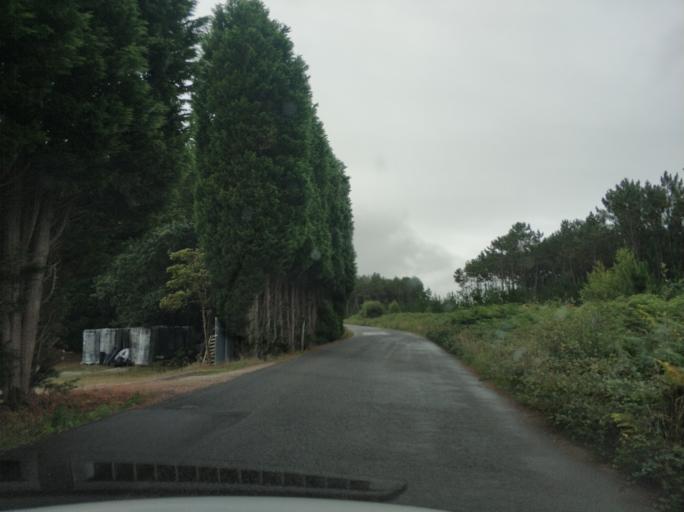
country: ES
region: Asturias
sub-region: Province of Asturias
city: Tineo
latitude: 43.5520
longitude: -6.4541
